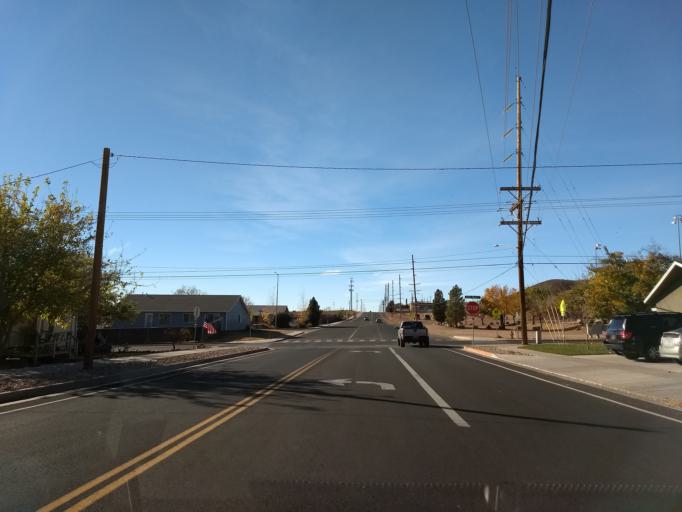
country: US
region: Utah
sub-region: Washington County
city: Hurricane
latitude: 37.1852
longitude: -113.2914
